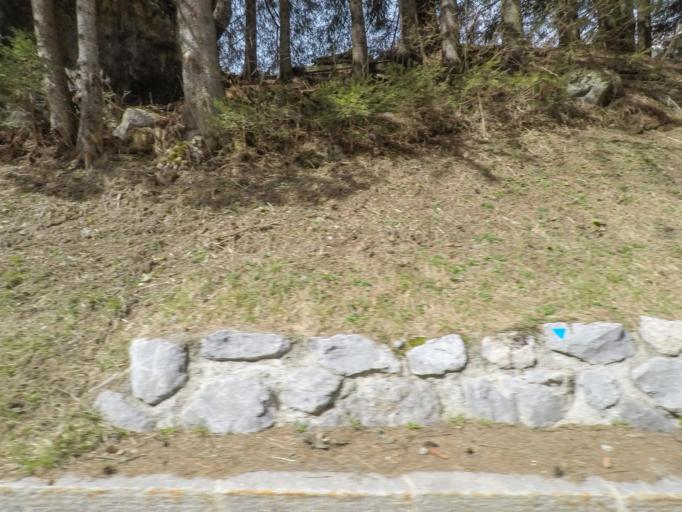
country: CH
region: Valais
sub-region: Saint-Maurice District
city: Salvan
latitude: 46.0376
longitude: 6.9368
